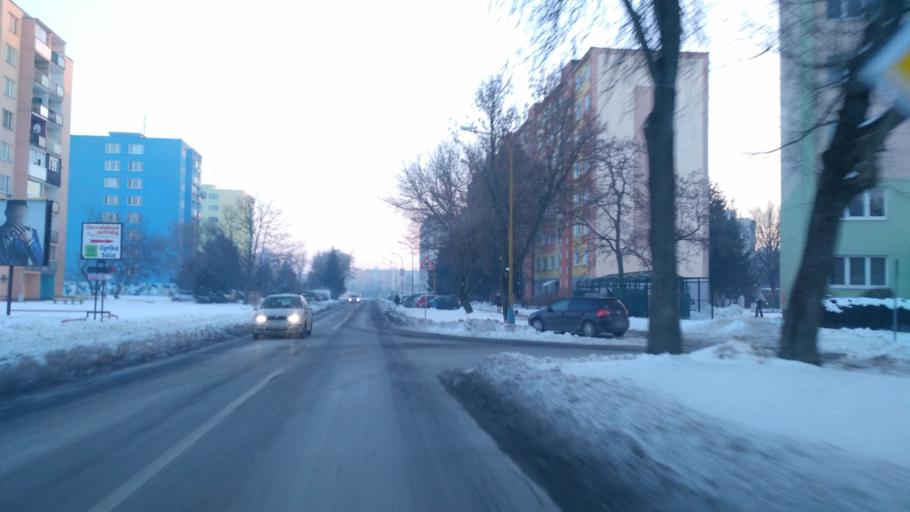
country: SK
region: Kosicky
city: Kosice
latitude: 48.7187
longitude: 21.2399
